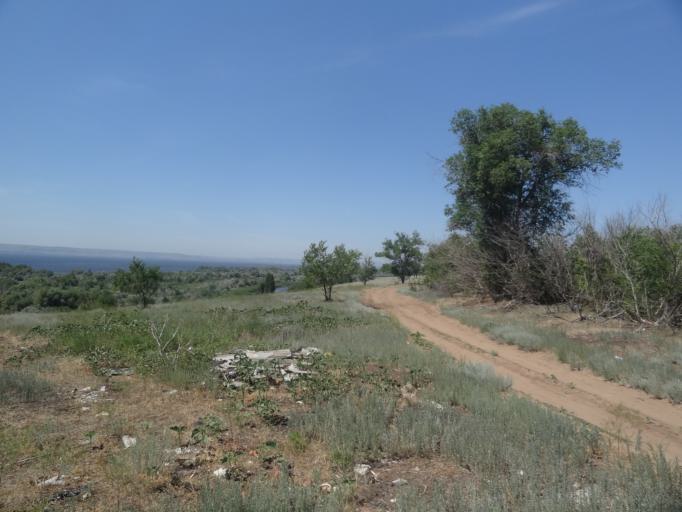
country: RU
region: Saratov
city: Krasnoarmeysk
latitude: 51.1270
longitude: 45.9415
